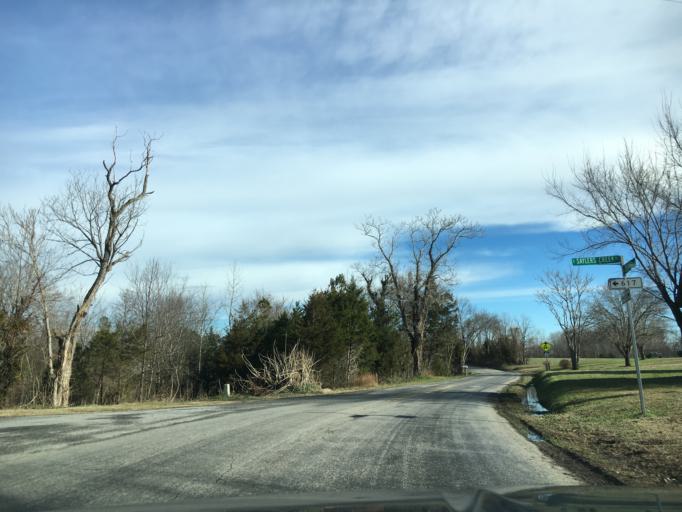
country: US
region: Virginia
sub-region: Nottoway County
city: Crewe
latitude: 37.3280
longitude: -78.1679
